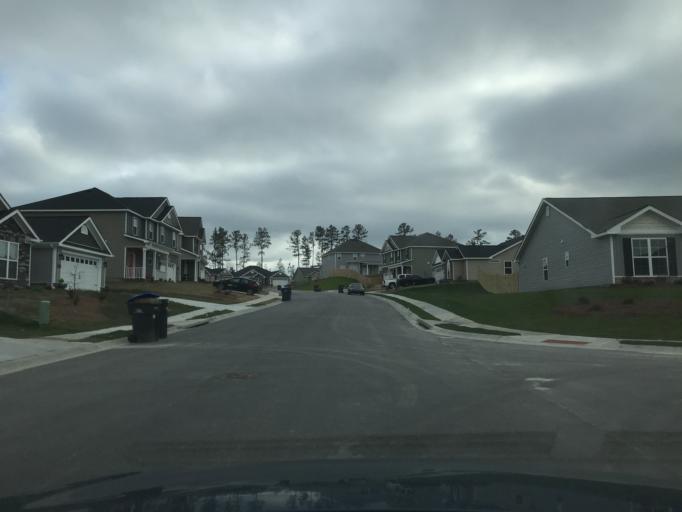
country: US
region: Georgia
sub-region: Columbia County
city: Grovetown
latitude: 33.4456
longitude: -82.1435
